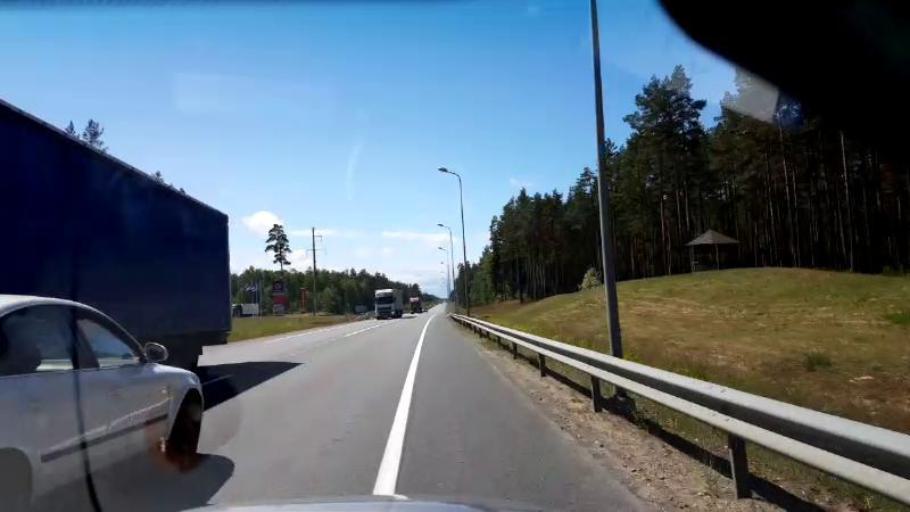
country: LV
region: Saulkrastu
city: Saulkrasti
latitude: 57.2268
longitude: 24.4184
